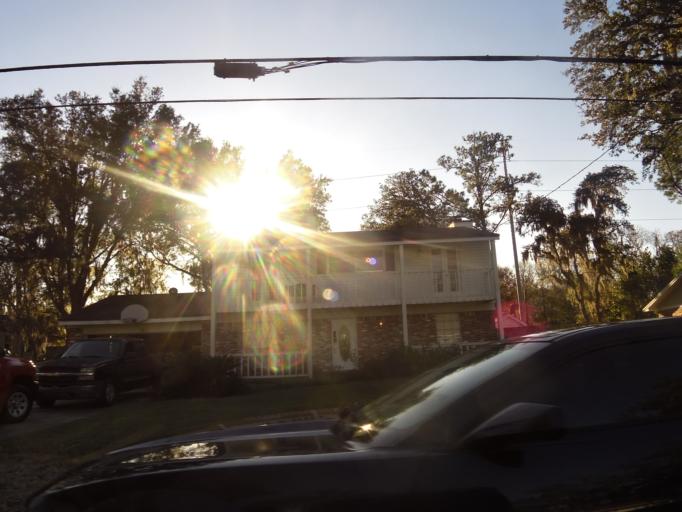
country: US
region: Florida
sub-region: Duval County
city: Jacksonville
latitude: 30.2255
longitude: -81.6008
